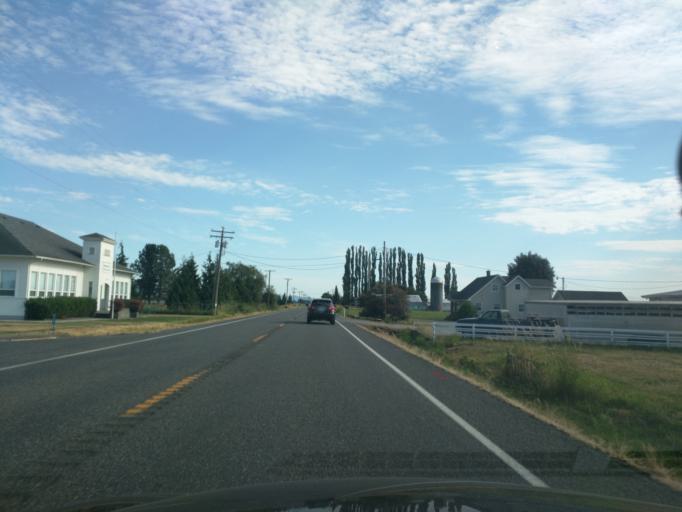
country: US
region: Washington
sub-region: Whatcom County
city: Lynden
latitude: 48.9826
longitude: -122.4852
